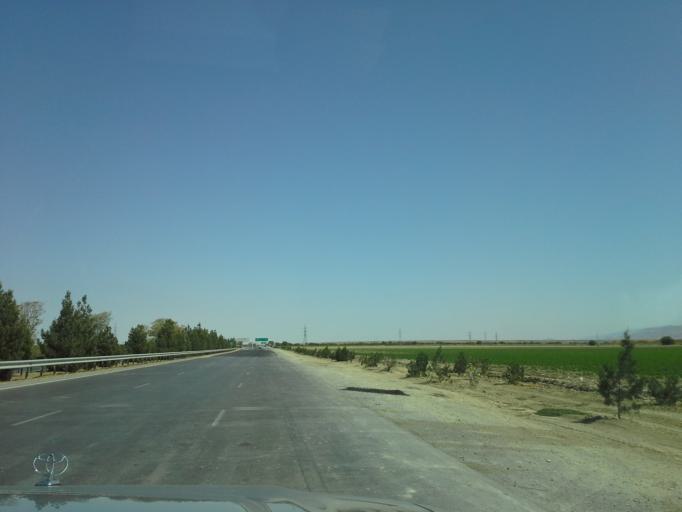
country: TM
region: Ahal
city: Annau
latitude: 37.9056
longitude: 58.5327
